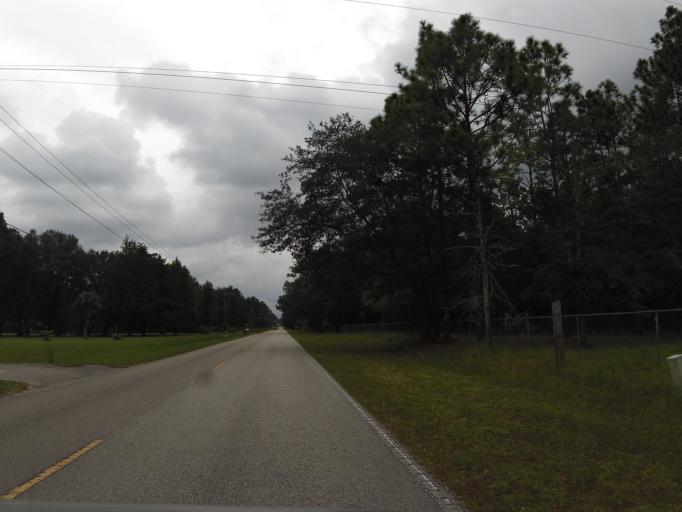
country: US
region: Florida
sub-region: Clay County
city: Middleburg
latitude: 30.1095
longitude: -81.9491
